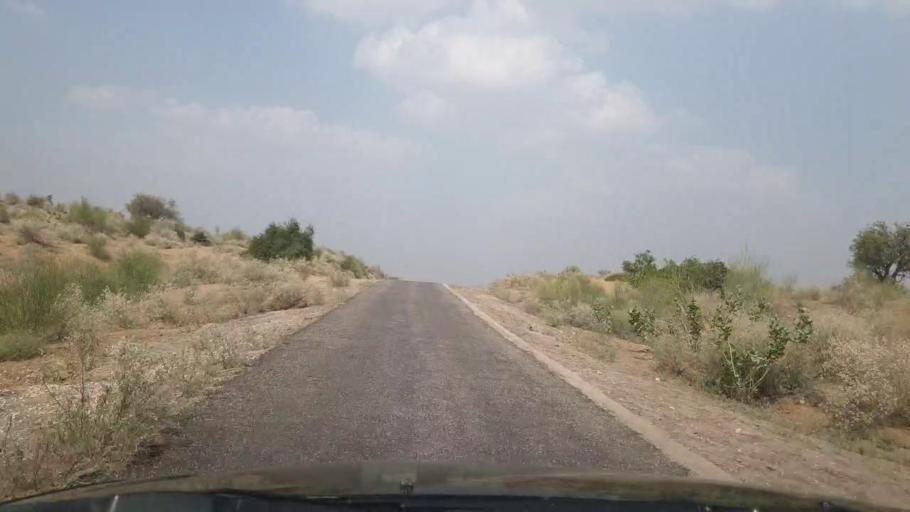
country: PK
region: Sindh
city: Islamkot
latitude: 24.8960
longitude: 70.5539
